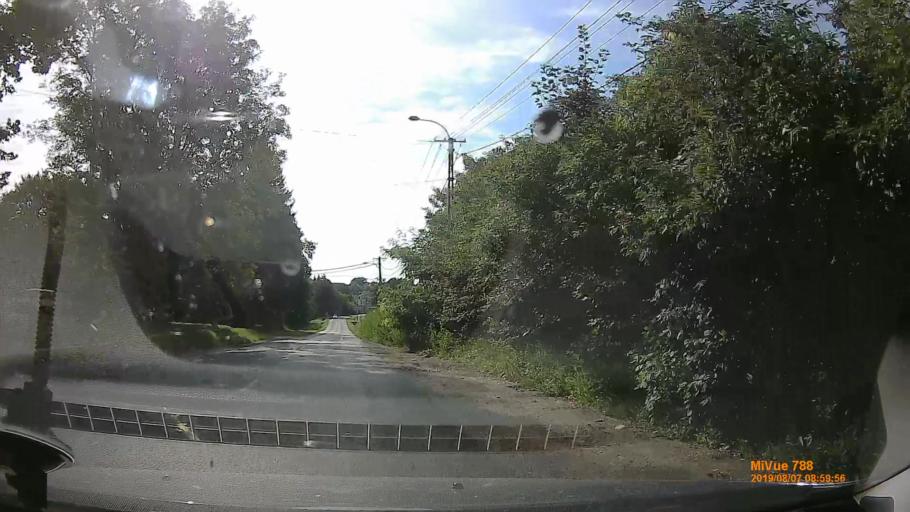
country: HU
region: Zala
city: Pacsa
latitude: 46.7307
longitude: 16.9423
